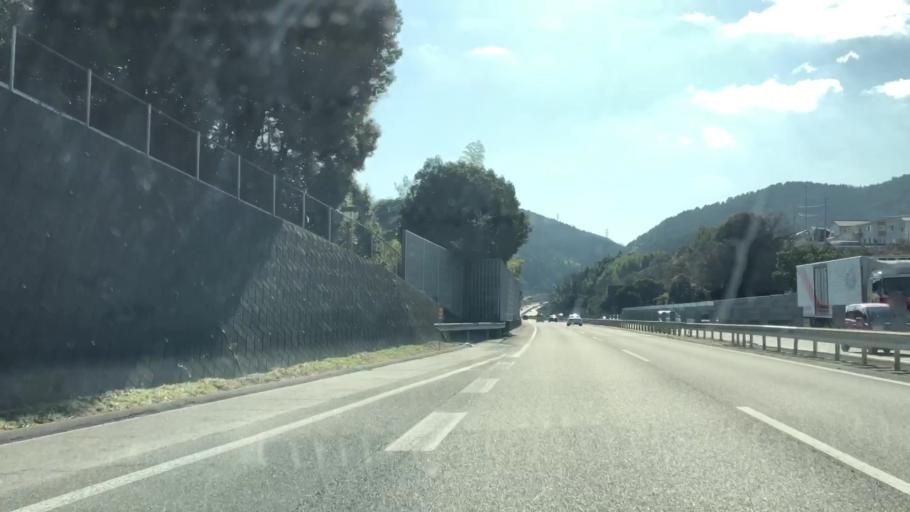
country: JP
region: Yamaguchi
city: Otake
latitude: 34.2405
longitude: 132.2151
